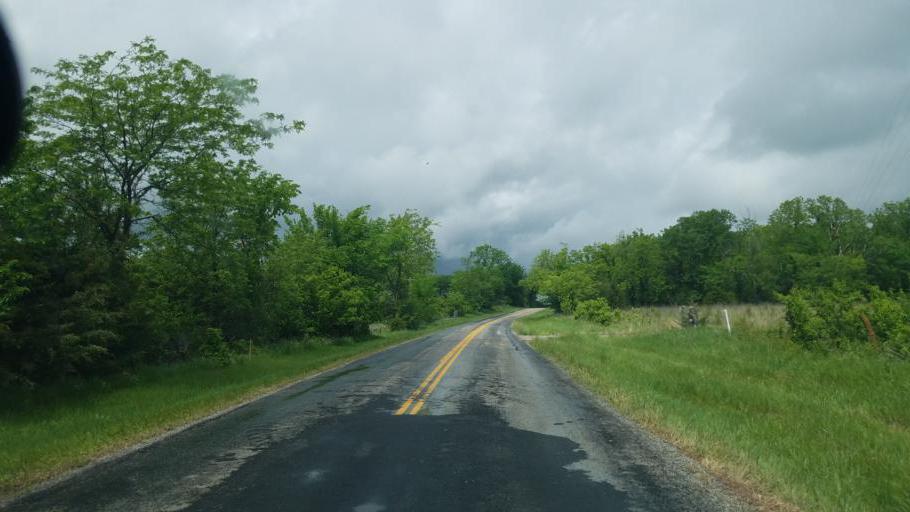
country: US
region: Missouri
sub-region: Mercer County
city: Princeton
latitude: 40.5224
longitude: -93.7175
